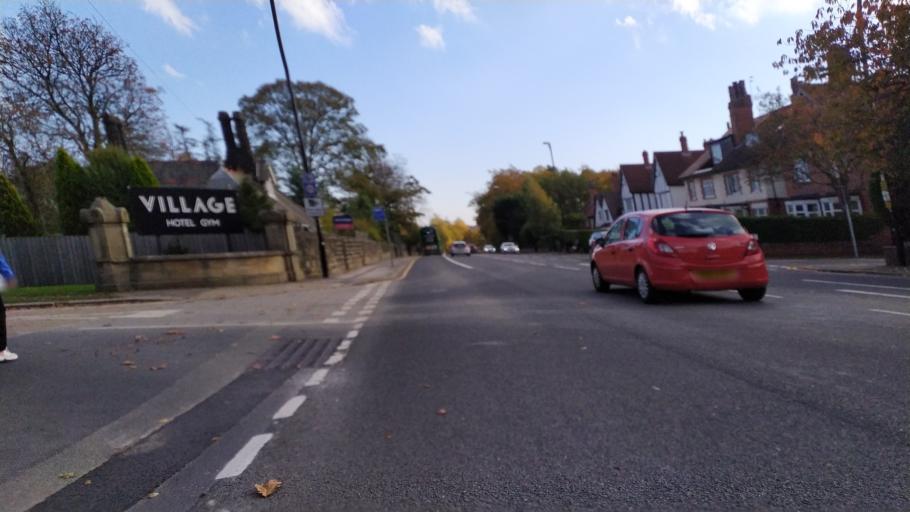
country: GB
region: England
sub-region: City and Borough of Leeds
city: Horsforth
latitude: 53.8327
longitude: -1.5914
